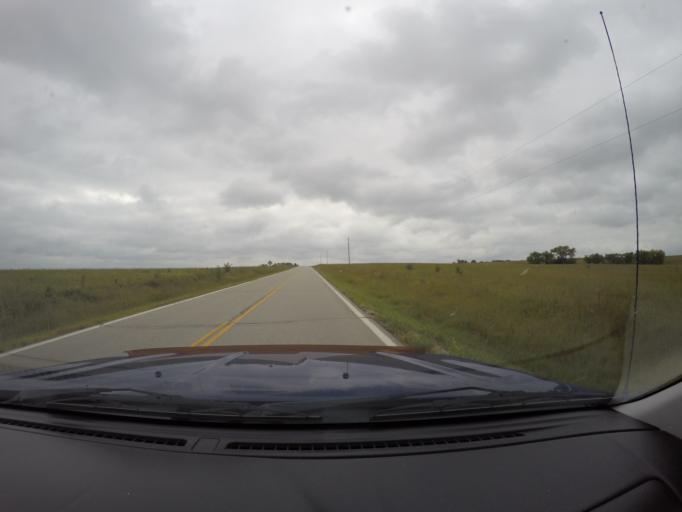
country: US
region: Kansas
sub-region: Morris County
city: Council Grove
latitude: 38.8407
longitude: -96.5054
